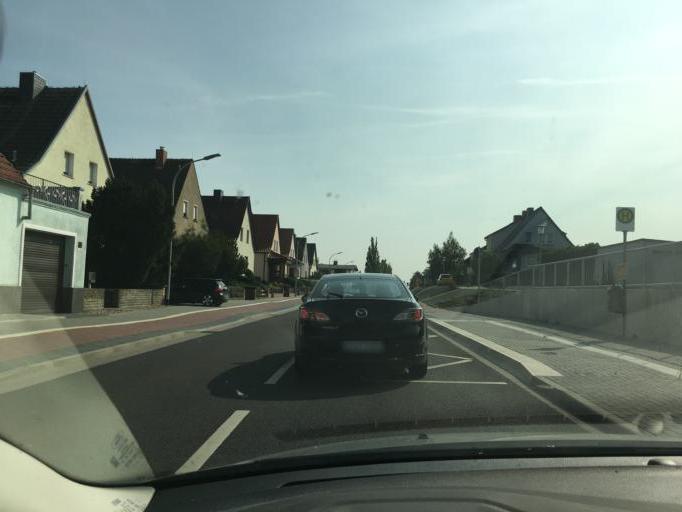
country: DE
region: Saxony-Anhalt
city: Calbe
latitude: 51.8904
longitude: 11.7696
